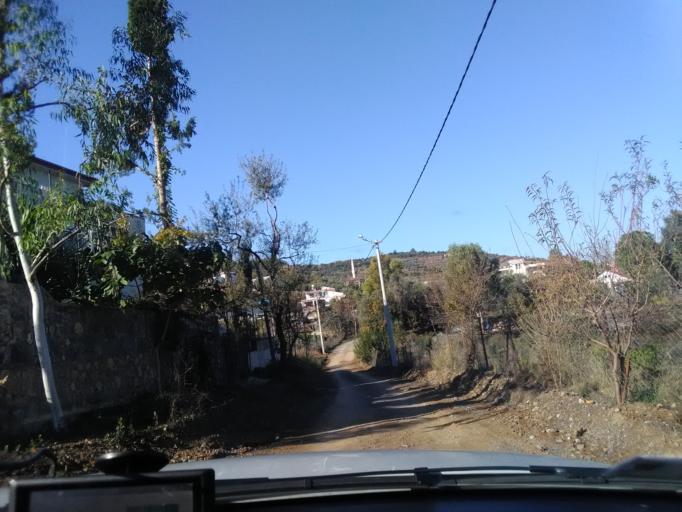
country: TR
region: Antalya
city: Gazipasa
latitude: 36.2467
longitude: 32.3415
